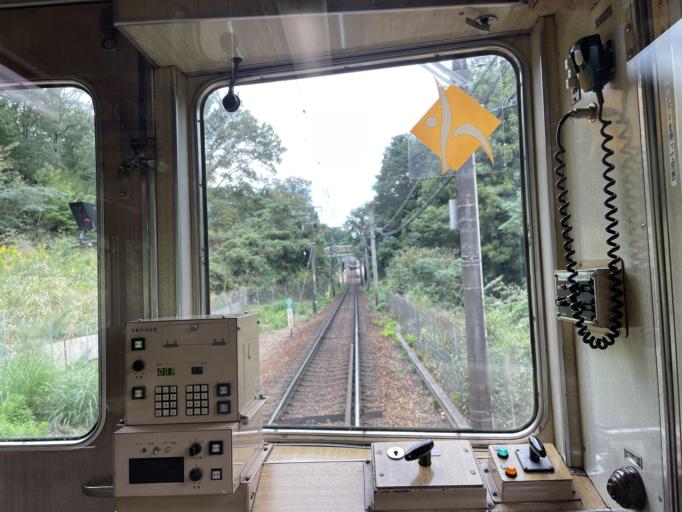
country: JP
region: Osaka
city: Ikeda
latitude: 34.8936
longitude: 135.4184
